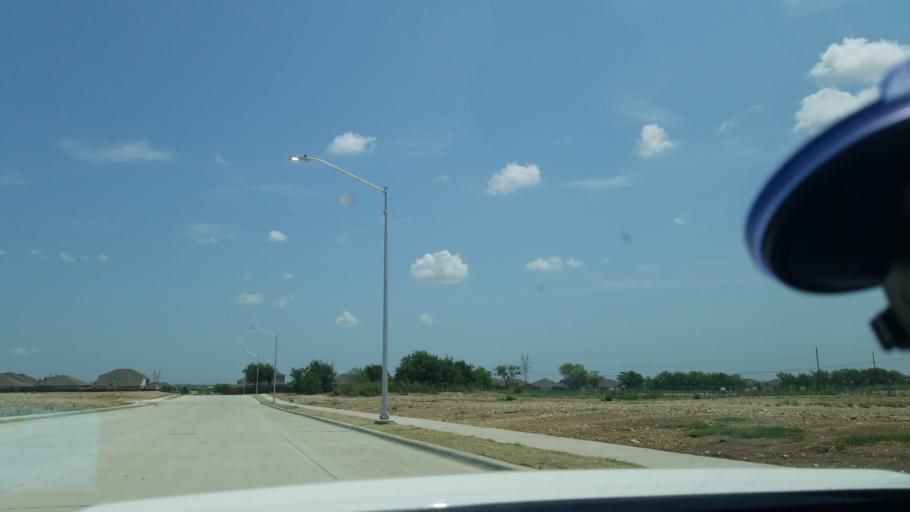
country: US
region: Texas
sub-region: Tarrant County
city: Saginaw
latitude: 32.9137
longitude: -97.3708
